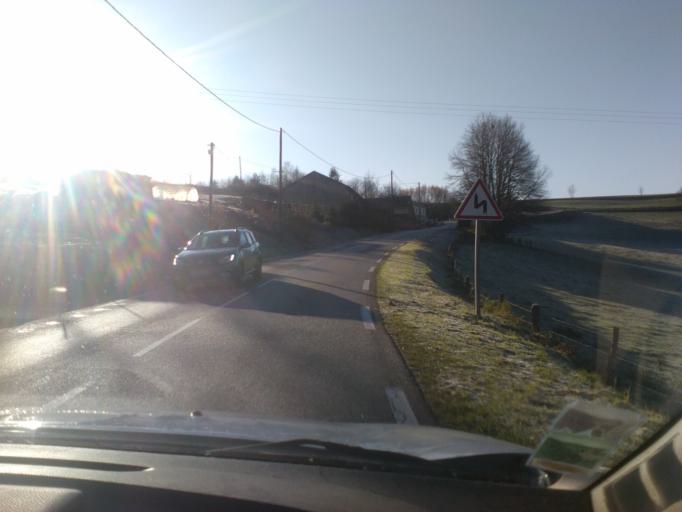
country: FR
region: Lorraine
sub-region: Departement des Vosges
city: Xertigny
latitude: 48.0372
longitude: 6.4154
